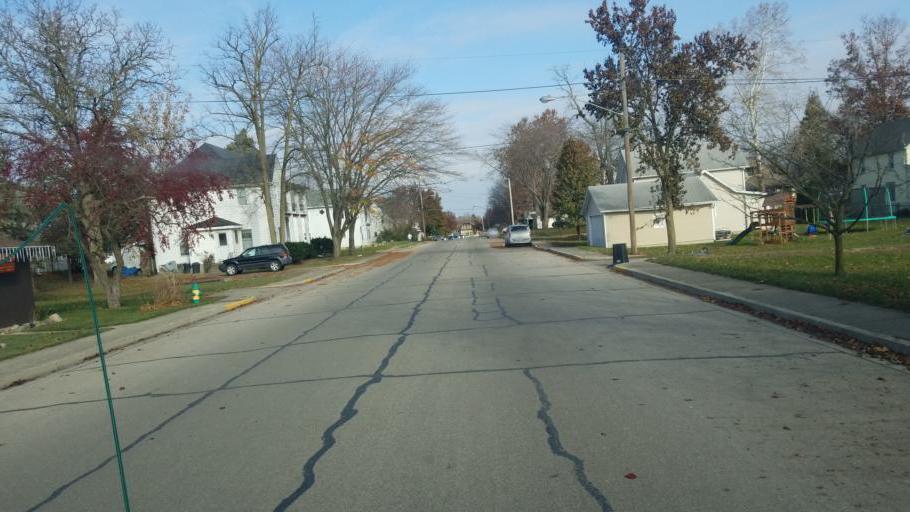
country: US
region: Indiana
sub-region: Adams County
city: Berne
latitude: 40.6542
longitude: -84.9512
